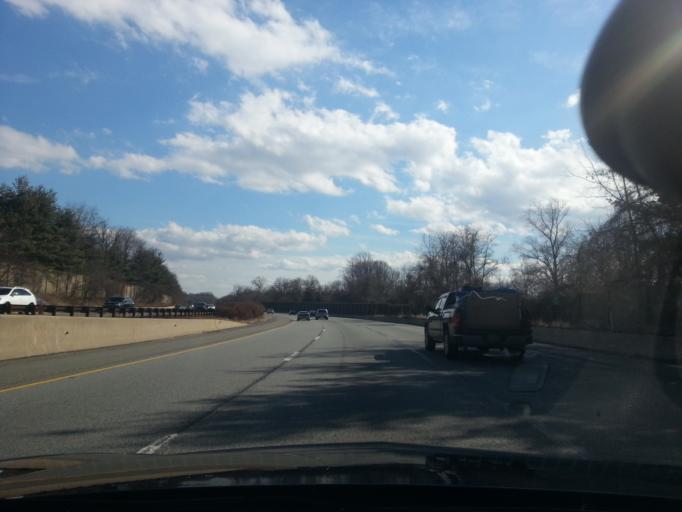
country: US
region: Pennsylvania
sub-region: Delaware County
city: Radnor
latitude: 40.0270
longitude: -75.3637
